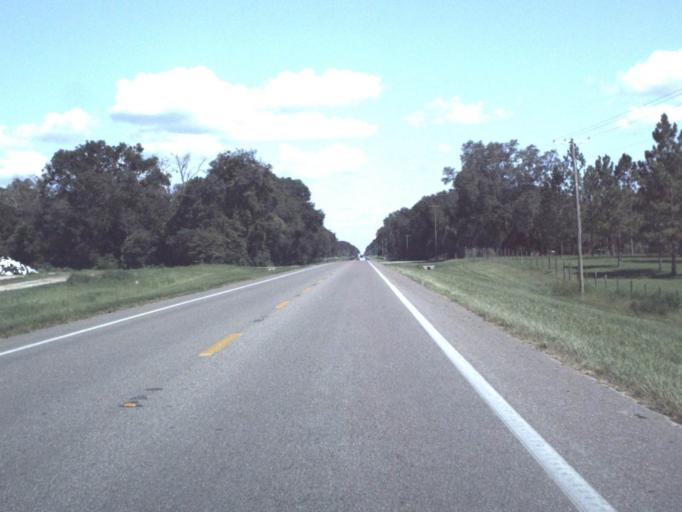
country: US
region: Florida
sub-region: Lafayette County
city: Mayo
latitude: 30.0366
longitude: -83.0677
